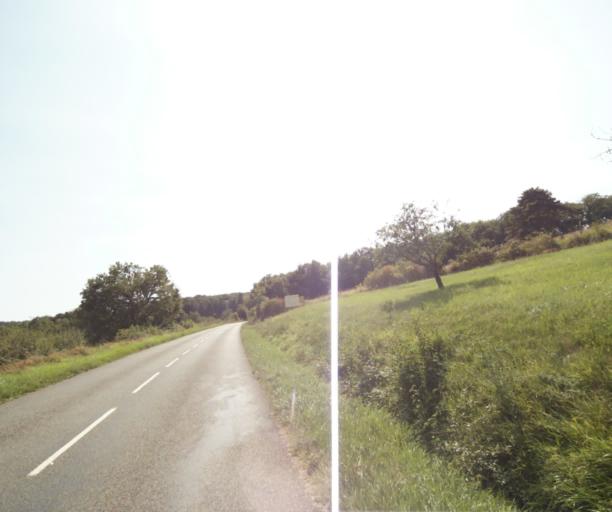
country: FR
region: Bourgogne
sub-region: Departement de Saone-et-Loire
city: Tournus
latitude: 46.5520
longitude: 4.8755
